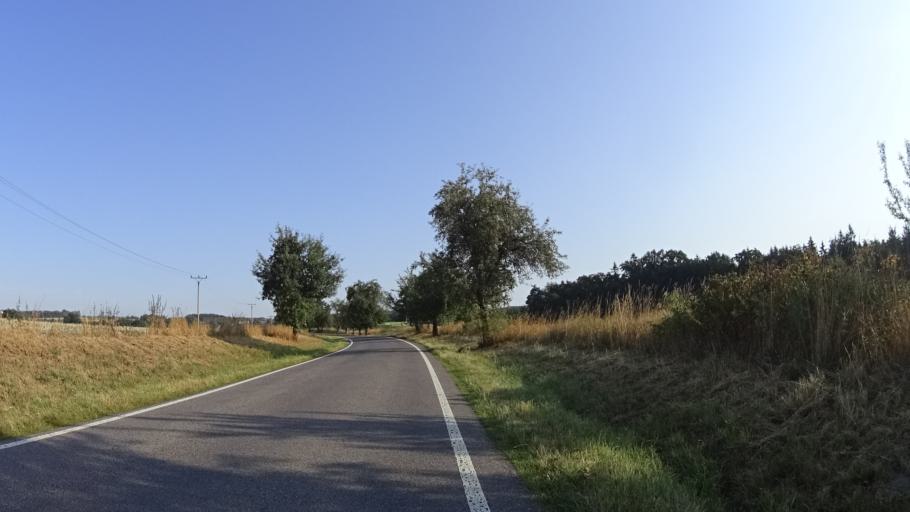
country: CZ
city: Ohrazenice
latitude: 50.6113
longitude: 15.1278
